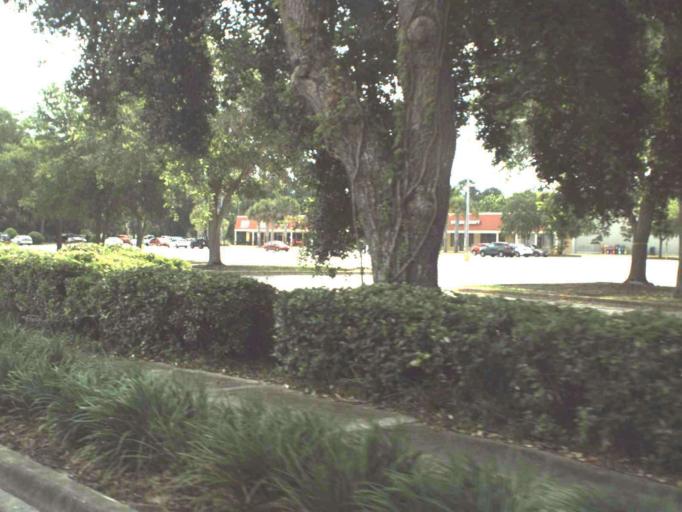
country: US
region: Florida
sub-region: Volusia County
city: New Smyrna Beach
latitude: 29.0151
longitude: -80.9407
